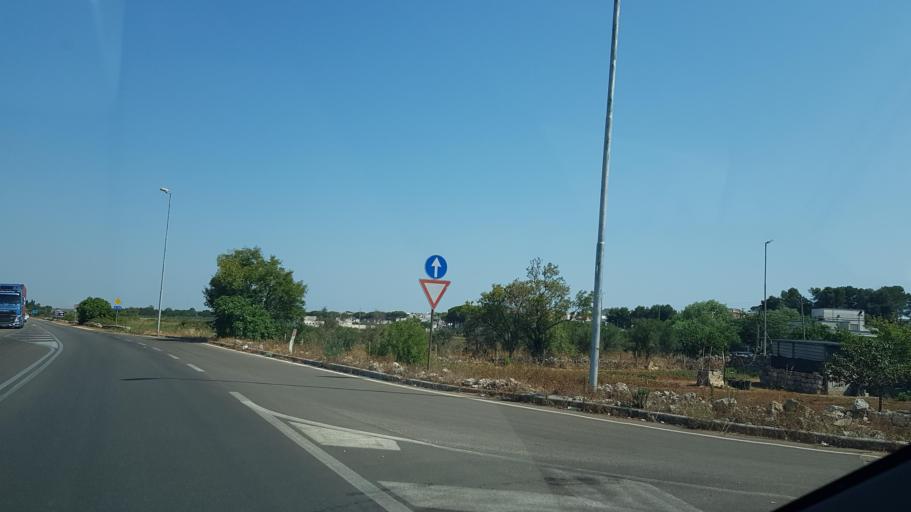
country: IT
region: Apulia
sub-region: Provincia di Lecce
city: Nociglia
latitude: 40.0311
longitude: 18.3247
